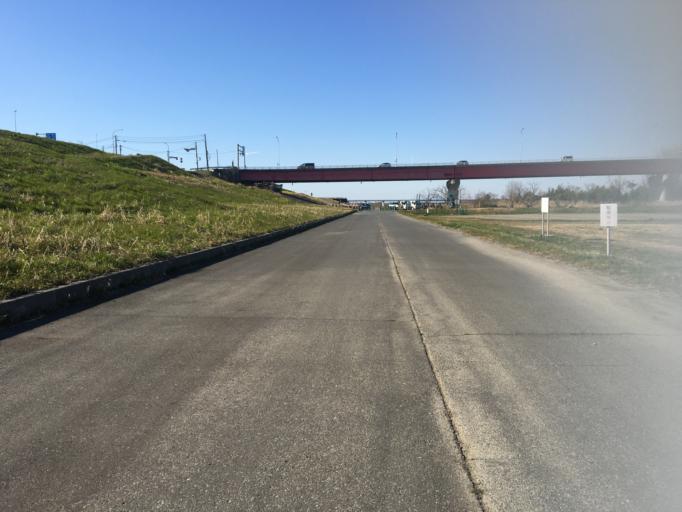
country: JP
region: Saitama
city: Shiki
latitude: 35.8336
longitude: 139.6052
